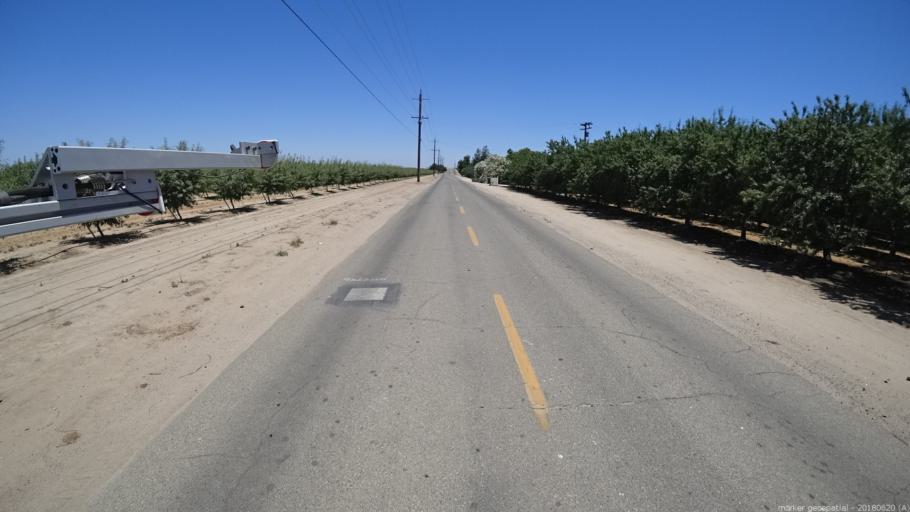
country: US
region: California
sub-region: Madera County
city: Parkwood
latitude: 36.9094
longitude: -120.0142
